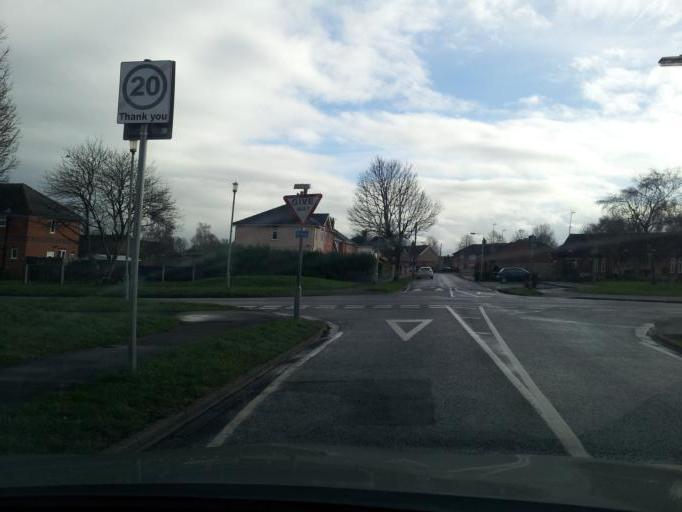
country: GB
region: England
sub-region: Nottinghamshire
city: Newark on Trent
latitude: 53.0653
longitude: -0.8093
